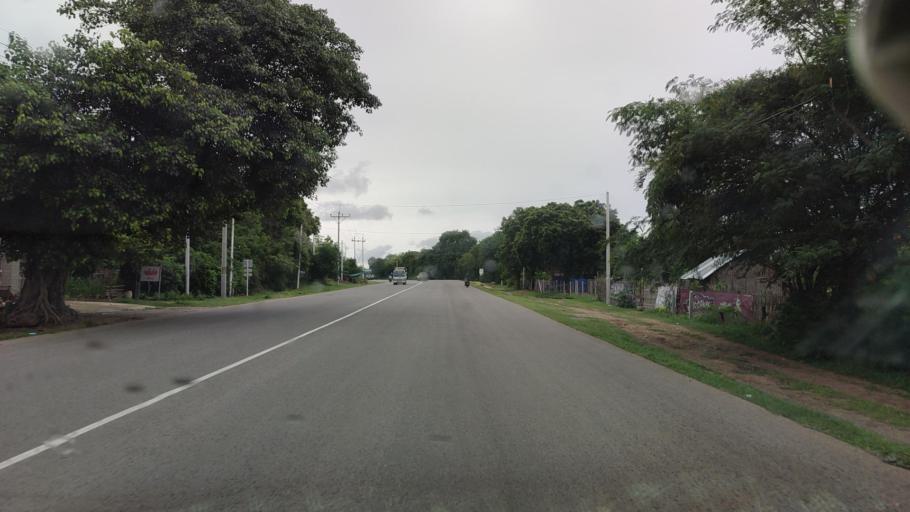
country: MM
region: Mandalay
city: Meiktila
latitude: 20.8169
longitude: 95.9064
